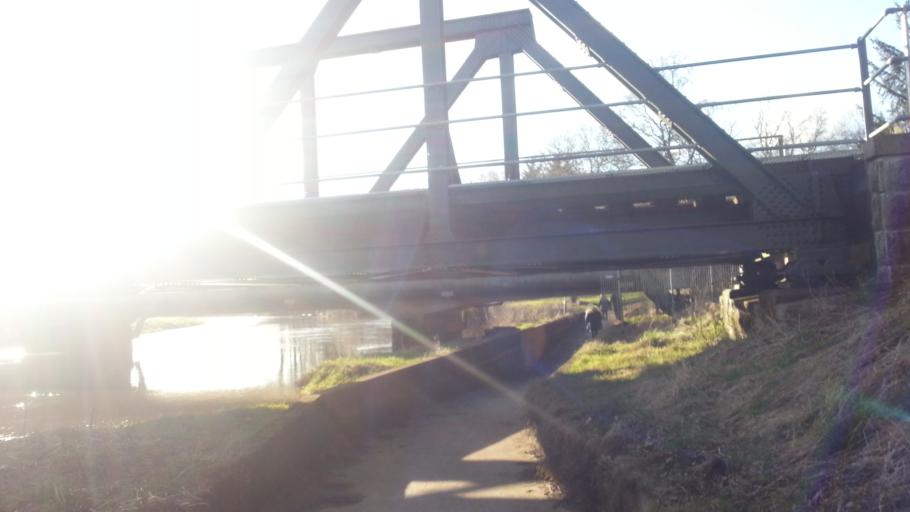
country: DK
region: South Denmark
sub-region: Varde Kommune
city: Varde
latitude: 55.6187
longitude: 8.4894
